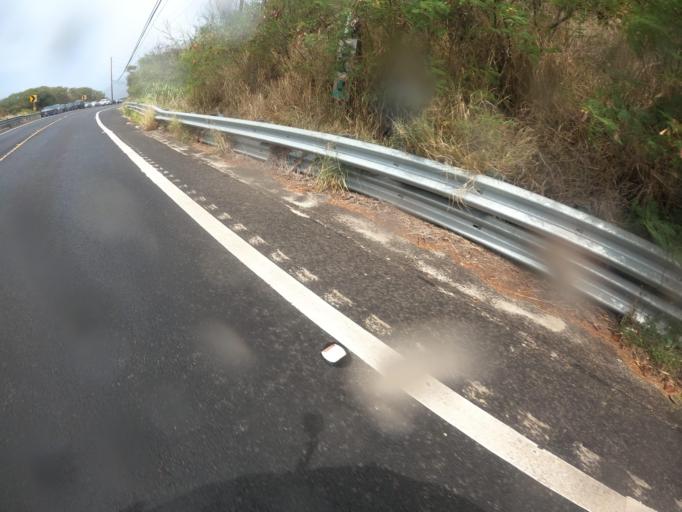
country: US
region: Hawaii
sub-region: Honolulu County
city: Makaha Valley
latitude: 21.5451
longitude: -158.2393
